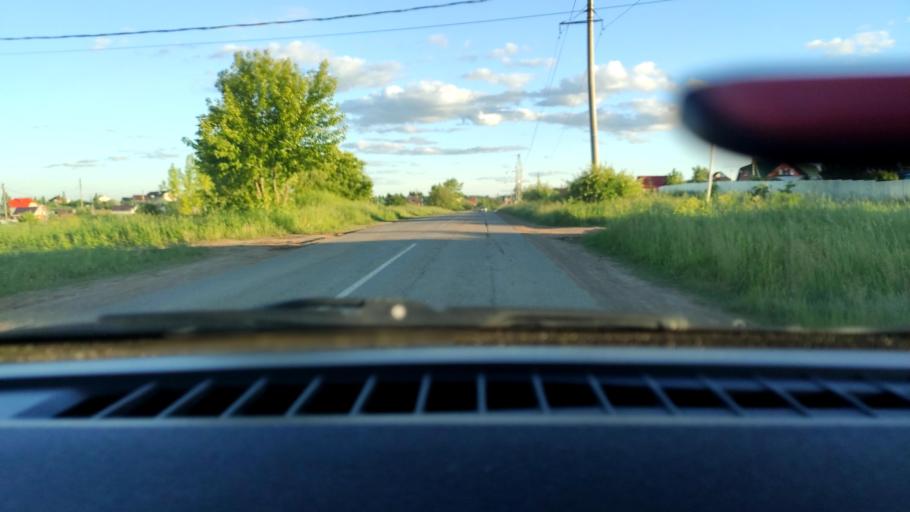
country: RU
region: Perm
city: Kultayevo
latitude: 57.9332
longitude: 55.8638
